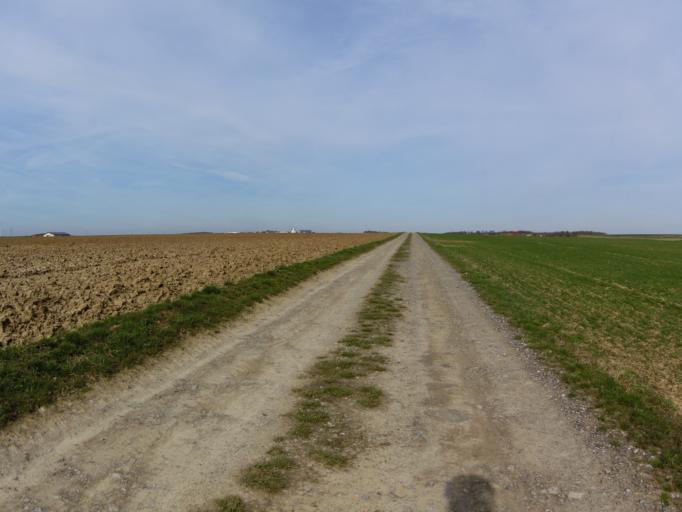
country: DE
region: Bavaria
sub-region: Regierungsbezirk Unterfranken
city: Biebelried
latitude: 49.7536
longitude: 10.0875
